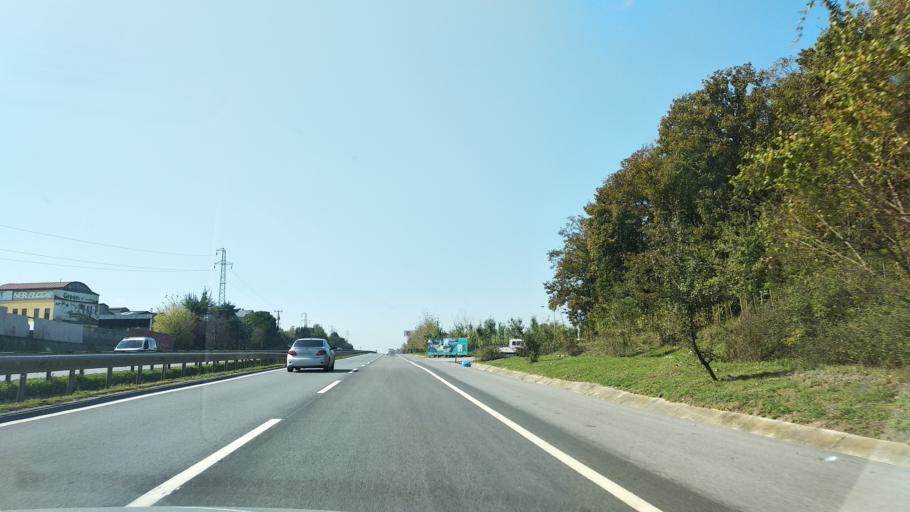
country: TR
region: Kocaeli
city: Derbent
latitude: 40.7316
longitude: 30.1651
